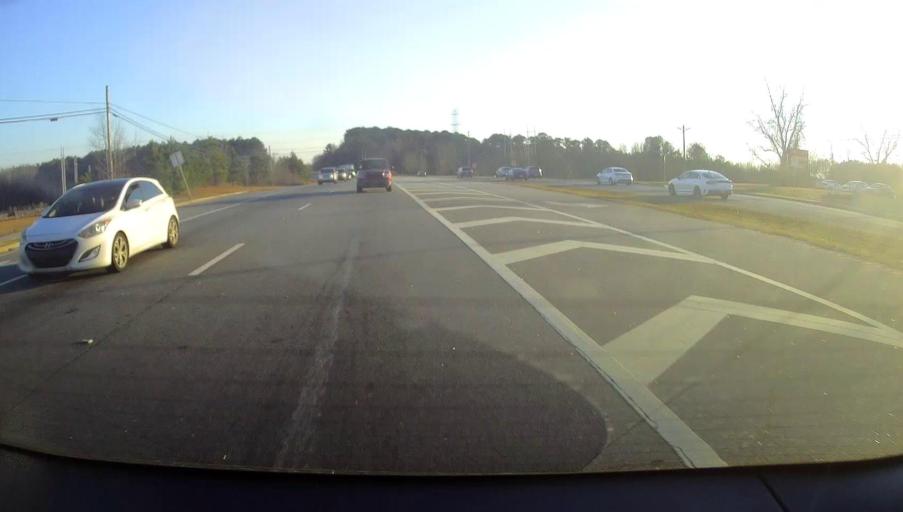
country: US
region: Georgia
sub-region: Fulton County
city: Fairburn
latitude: 33.5353
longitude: -84.5769
